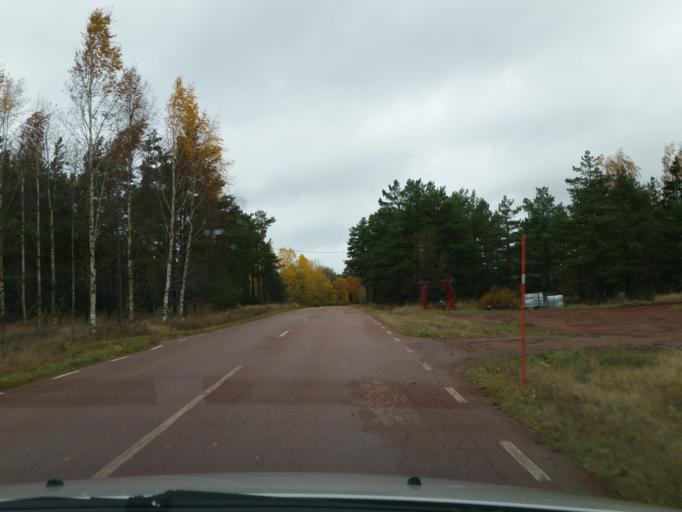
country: AX
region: Alands landsbygd
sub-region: Lumparland
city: Lumparland
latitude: 60.1232
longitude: 20.2414
